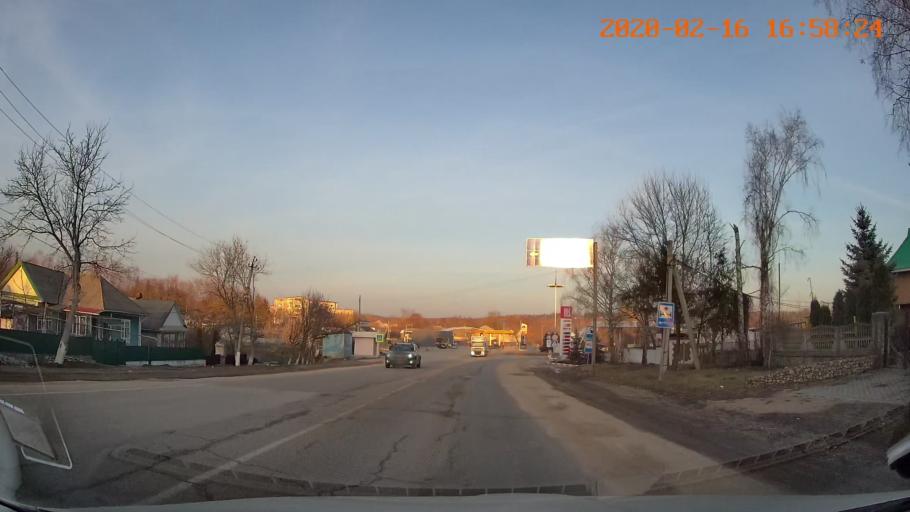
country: MD
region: Briceni
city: Briceni
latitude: 48.3503
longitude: 27.0827
